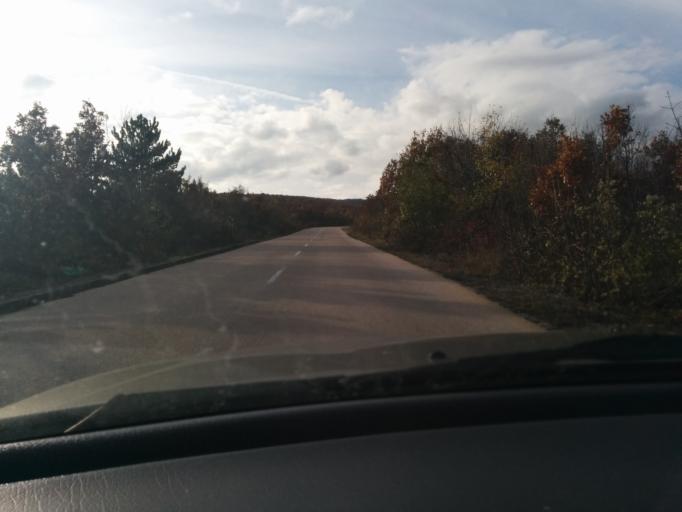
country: HR
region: Splitsko-Dalmatinska
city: Hrvace
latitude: 43.7575
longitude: 16.5844
